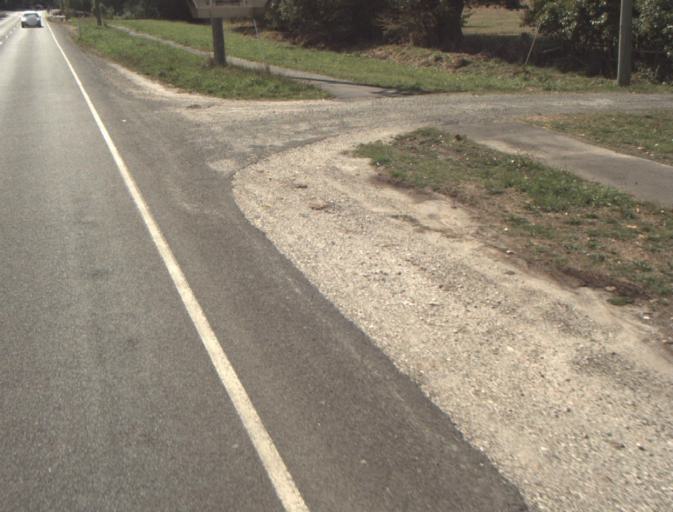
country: AU
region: Tasmania
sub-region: Launceston
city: Mayfield
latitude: -41.2569
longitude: 147.2171
